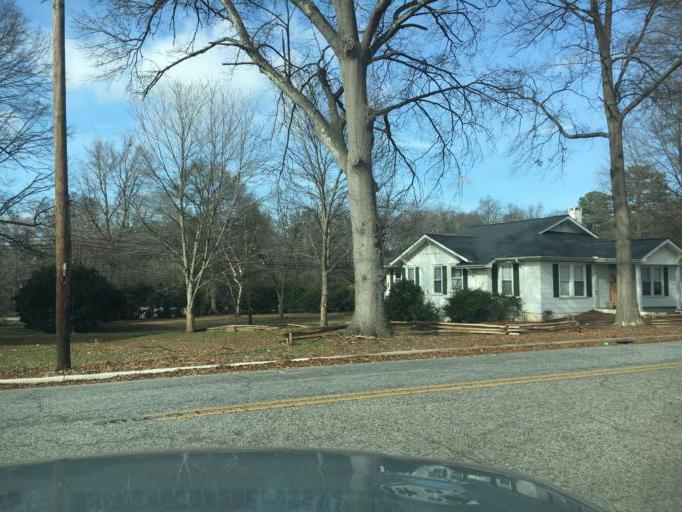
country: US
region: South Carolina
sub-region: Spartanburg County
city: Inman
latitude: 35.0438
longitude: -82.0961
